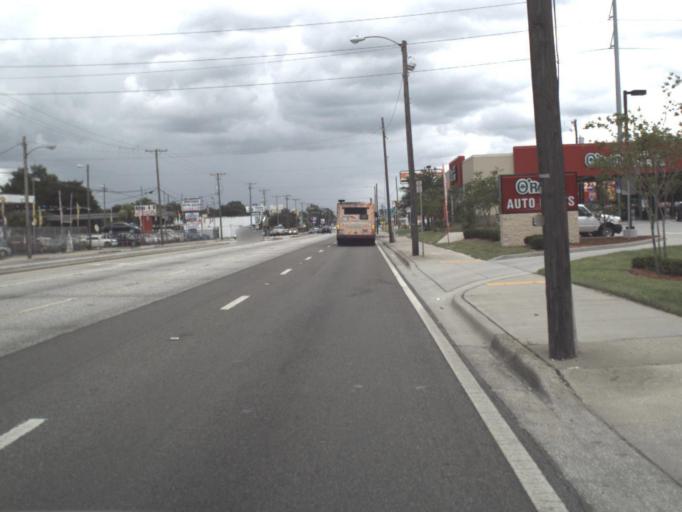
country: US
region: Florida
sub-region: Hillsborough County
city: East Lake-Orient Park
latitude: 27.9960
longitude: -82.4194
